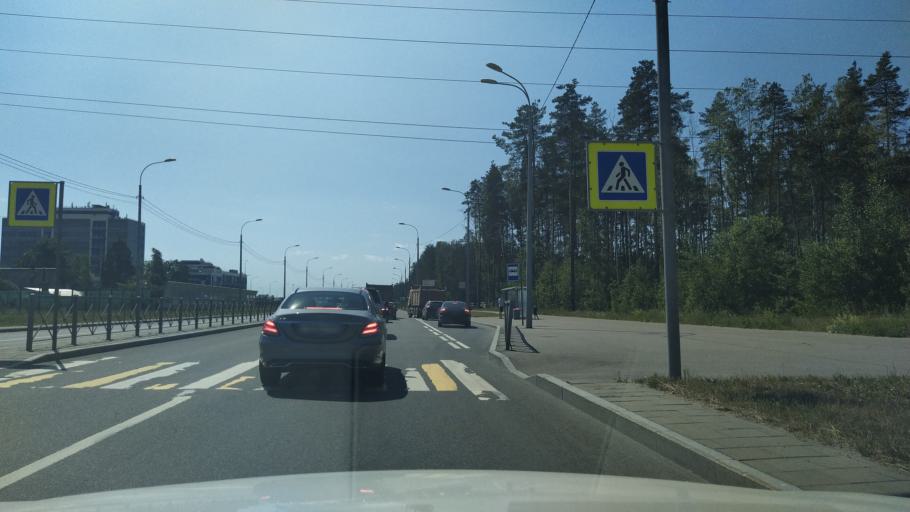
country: RU
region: St.-Petersburg
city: Pargolovo
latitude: 60.0560
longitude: 30.2362
